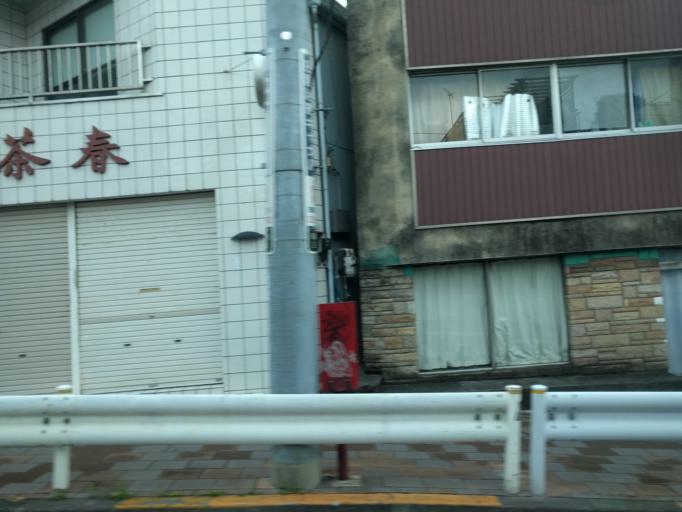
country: JP
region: Kanagawa
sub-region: Kawasaki-shi
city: Kawasaki
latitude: 35.5956
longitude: 139.6704
